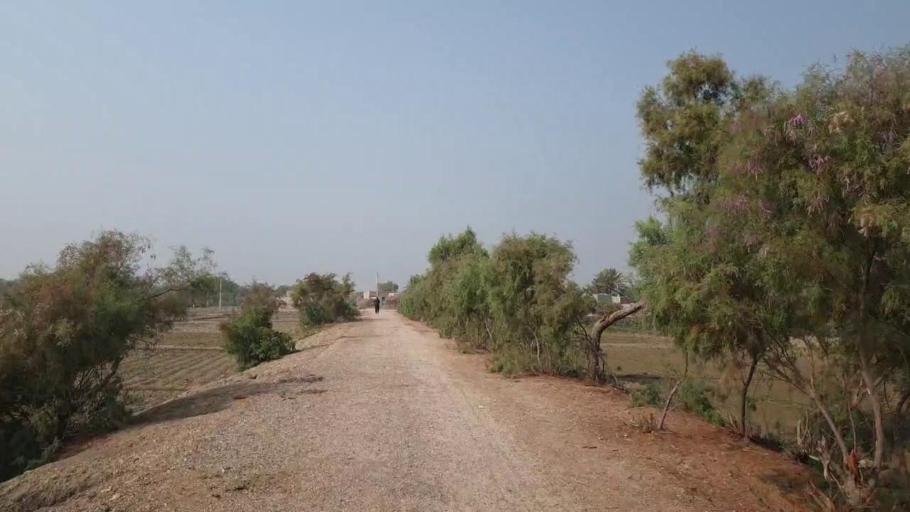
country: PK
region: Sindh
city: Bhan
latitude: 26.4527
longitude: 67.7353
